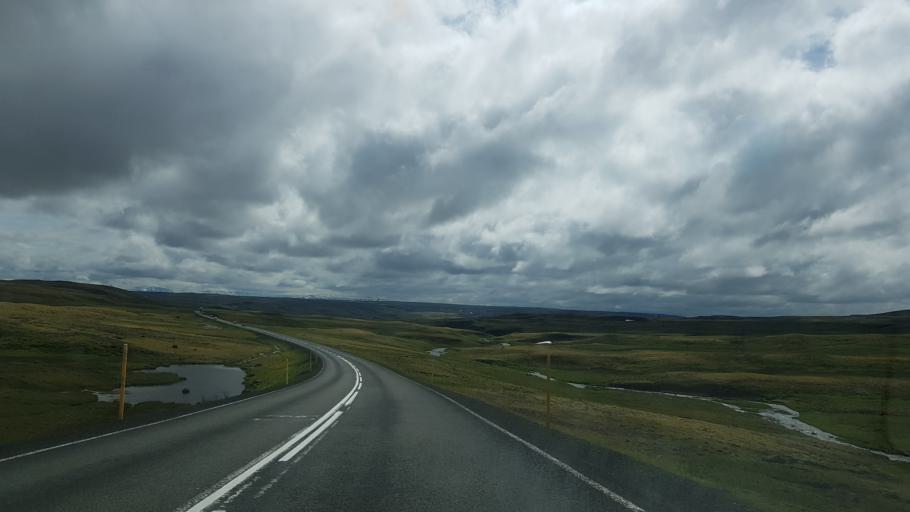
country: IS
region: West
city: Borgarnes
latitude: 64.9711
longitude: -21.0675
